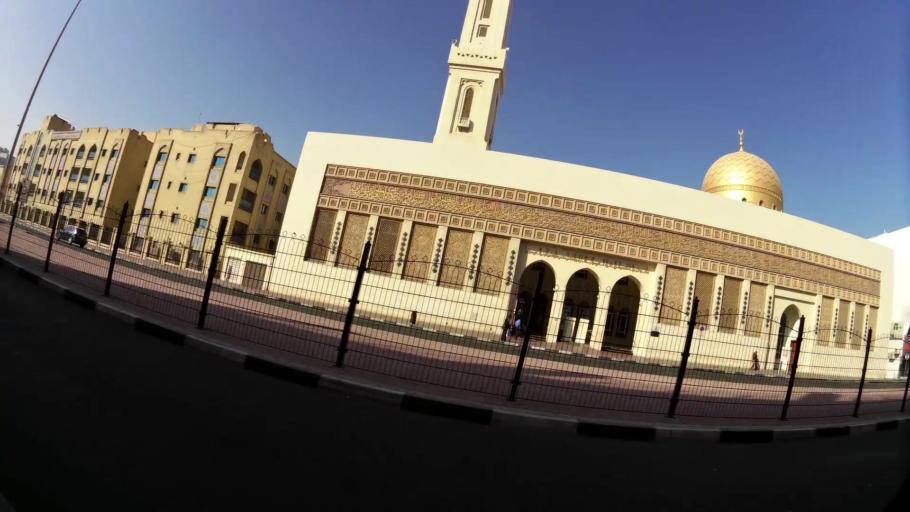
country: AE
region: Ash Shariqah
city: Sharjah
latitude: 25.2540
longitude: 55.3061
